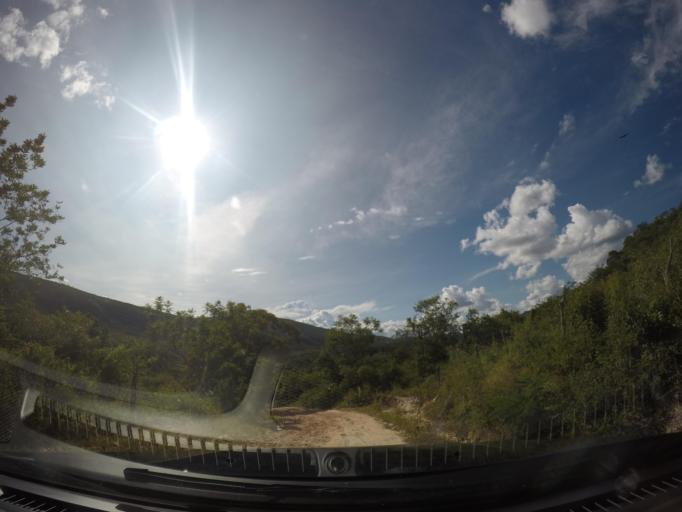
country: BR
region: Bahia
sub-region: Livramento Do Brumado
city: Livramento do Brumado
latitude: -13.2148
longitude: -41.6053
